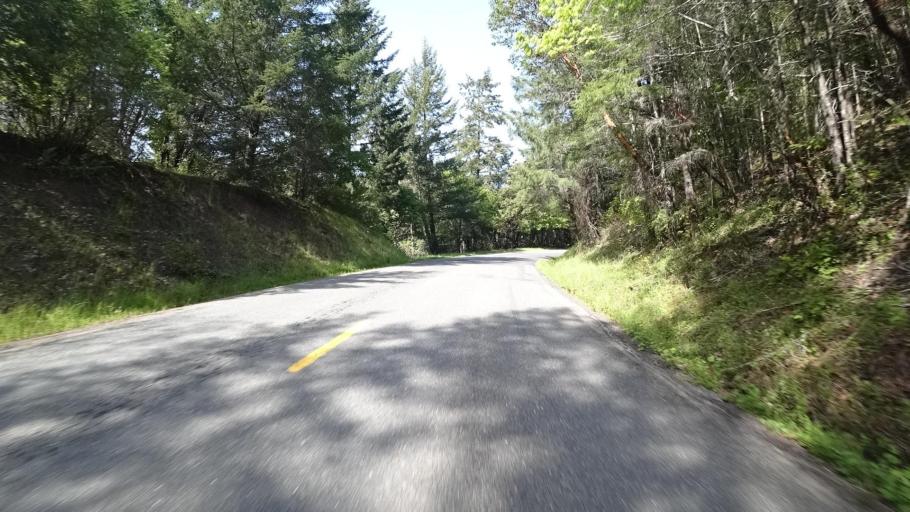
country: US
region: California
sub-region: Humboldt County
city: Rio Dell
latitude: 40.4641
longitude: -123.8043
